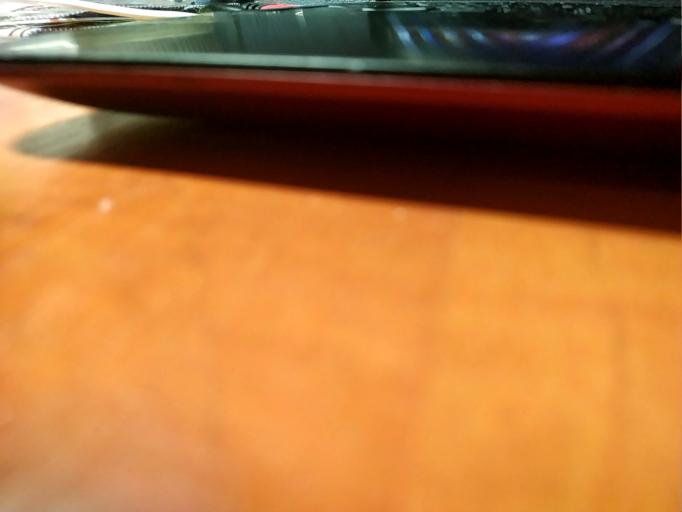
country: RU
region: Tverskaya
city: Vasil'yevskiy Mokh
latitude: 57.1738
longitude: 35.9495
